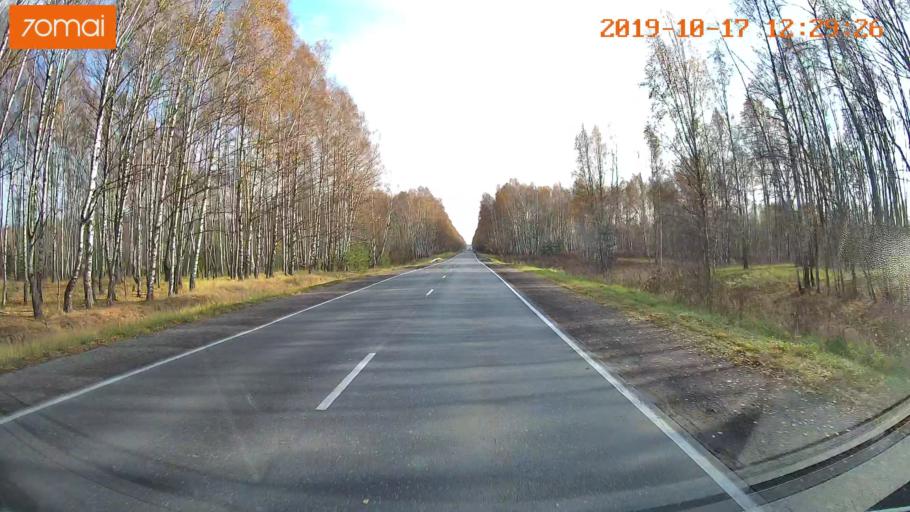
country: RU
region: Rjazan
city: Syntul
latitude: 54.9817
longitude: 41.2921
